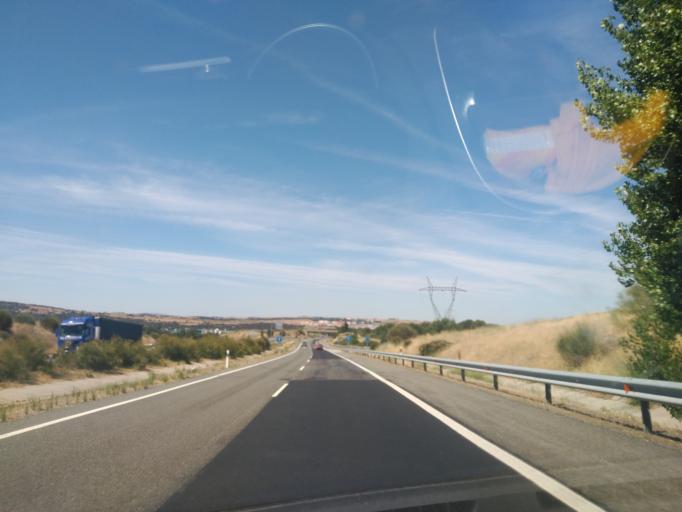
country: ES
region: Castille and Leon
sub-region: Provincia de Salamanca
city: Fuentes de Bejar
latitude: 40.4986
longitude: -5.6754
